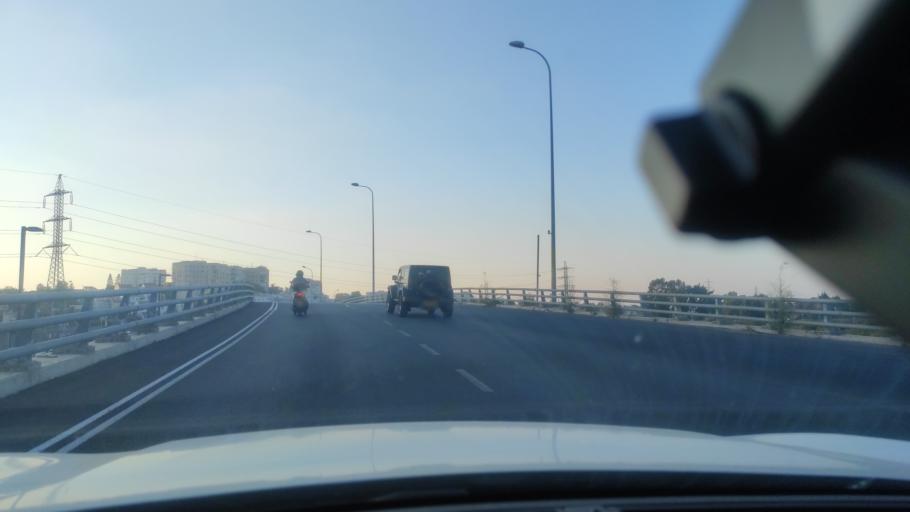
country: IL
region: Tel Aviv
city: Herzliyya
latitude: 32.1617
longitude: 34.8188
